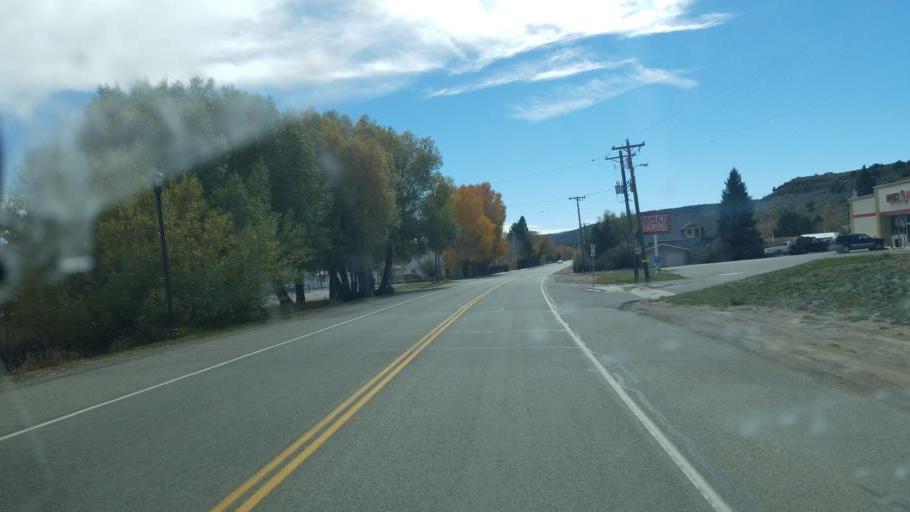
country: US
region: Colorado
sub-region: Costilla County
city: San Luis
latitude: 37.2063
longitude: -105.4251
